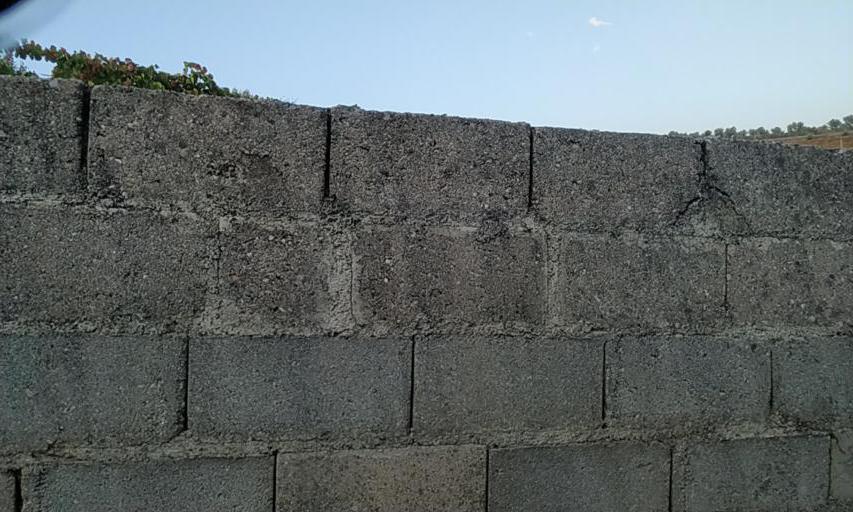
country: PT
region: Vila Real
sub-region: Peso da Regua
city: Godim
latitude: 41.1544
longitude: -7.8172
